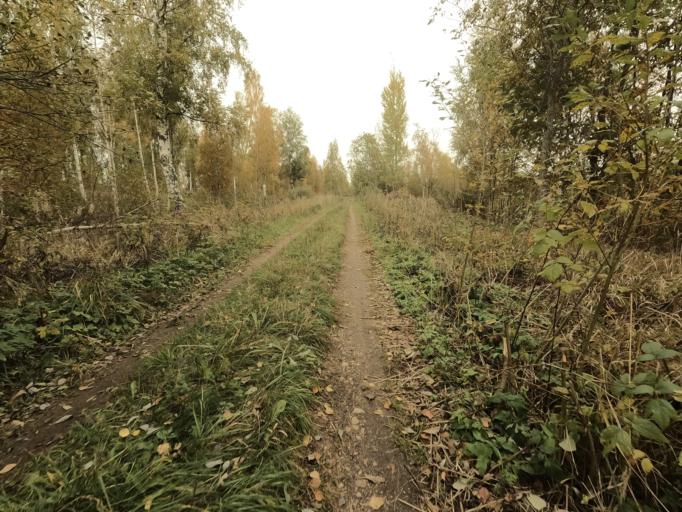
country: RU
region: Novgorod
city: Pankovka
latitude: 58.8690
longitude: 30.9356
